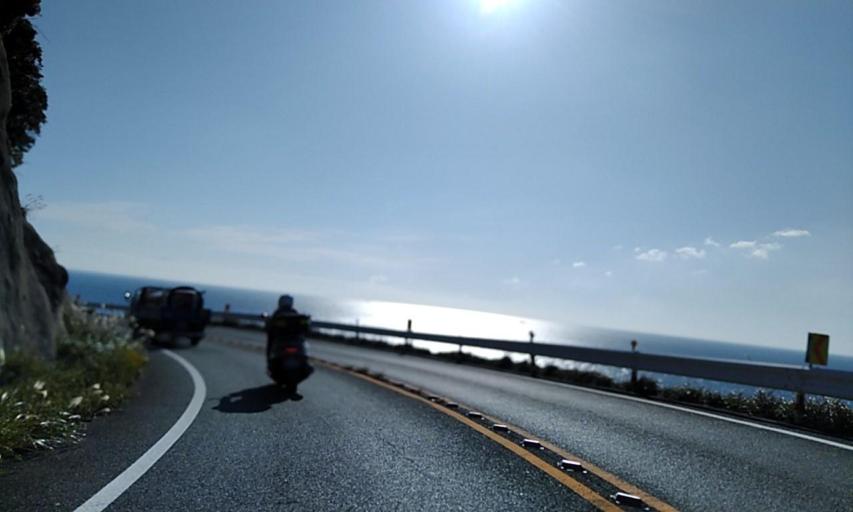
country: JP
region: Aichi
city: Toyohama
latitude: 34.5791
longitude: 137.0362
